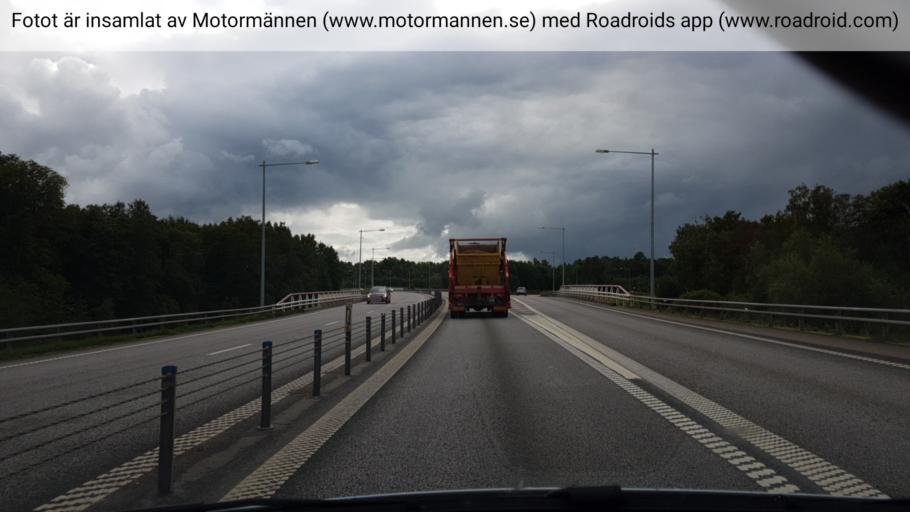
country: SE
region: Vaestra Goetaland
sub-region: Skovde Kommun
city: Skoevde
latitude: 58.3708
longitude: 13.8549
